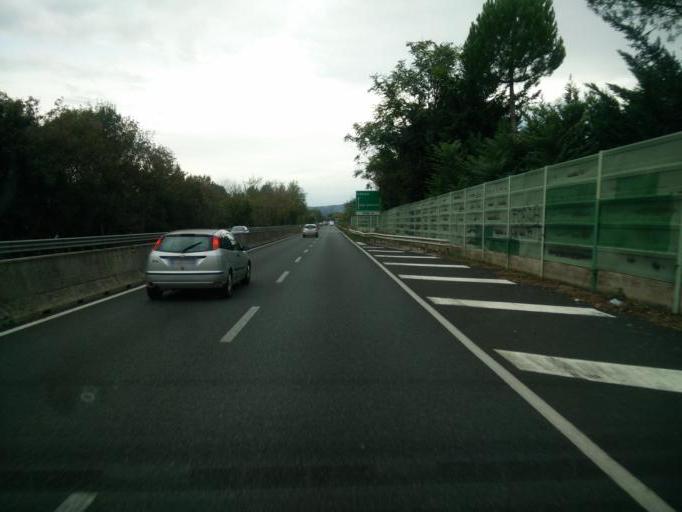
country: IT
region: Tuscany
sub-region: Province of Florence
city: San Casciano in Val di Pesa
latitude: 43.6167
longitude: 11.1884
